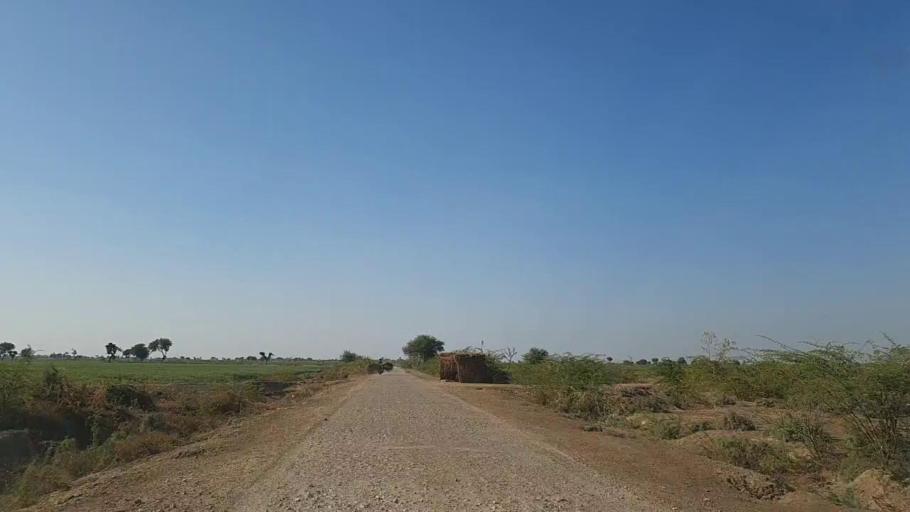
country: PK
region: Sindh
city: Samaro
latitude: 25.3663
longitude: 69.3829
